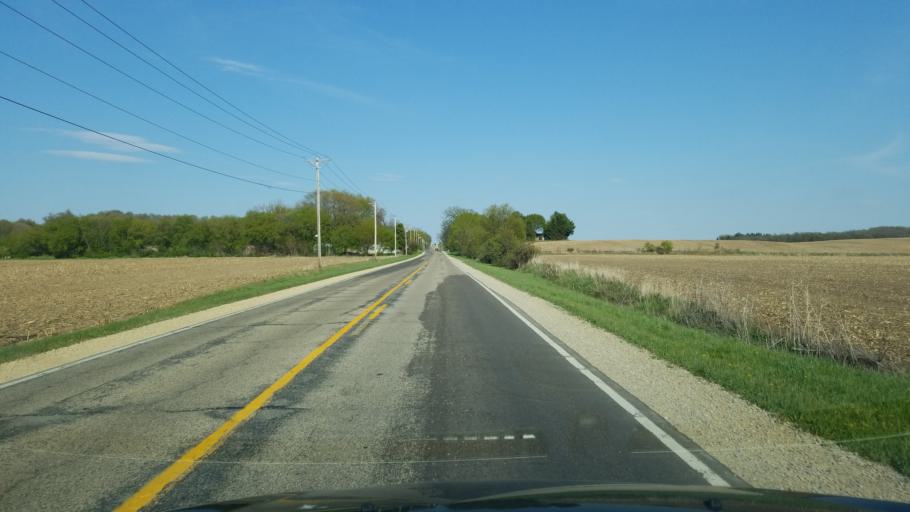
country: US
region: Wisconsin
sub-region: Dane County
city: Oregon
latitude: 42.9290
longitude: -89.4310
